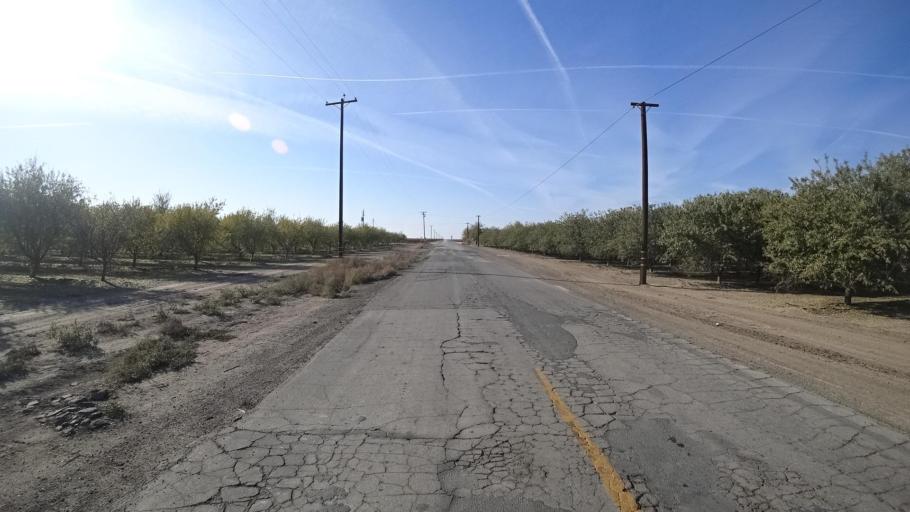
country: US
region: California
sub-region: Kern County
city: Wasco
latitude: 35.7029
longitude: -119.3823
